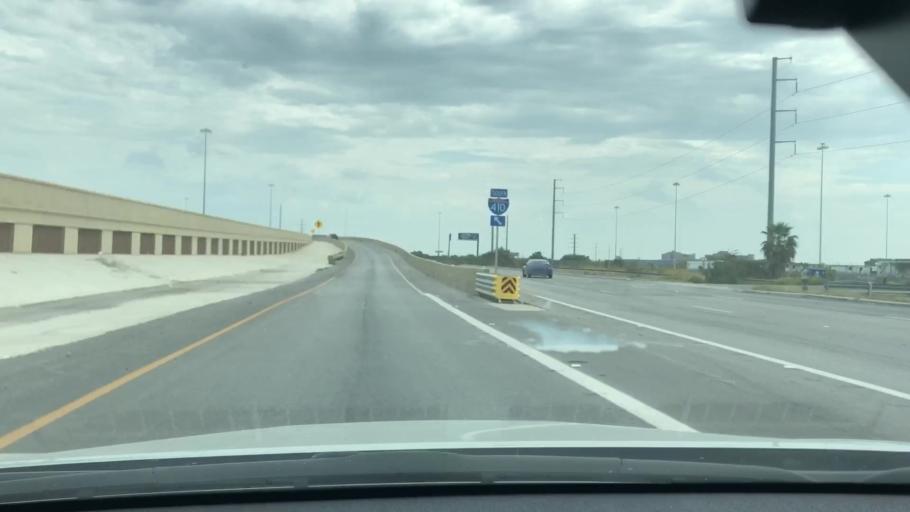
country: US
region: Texas
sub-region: Bexar County
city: Kirby
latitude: 29.4786
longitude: -98.4020
